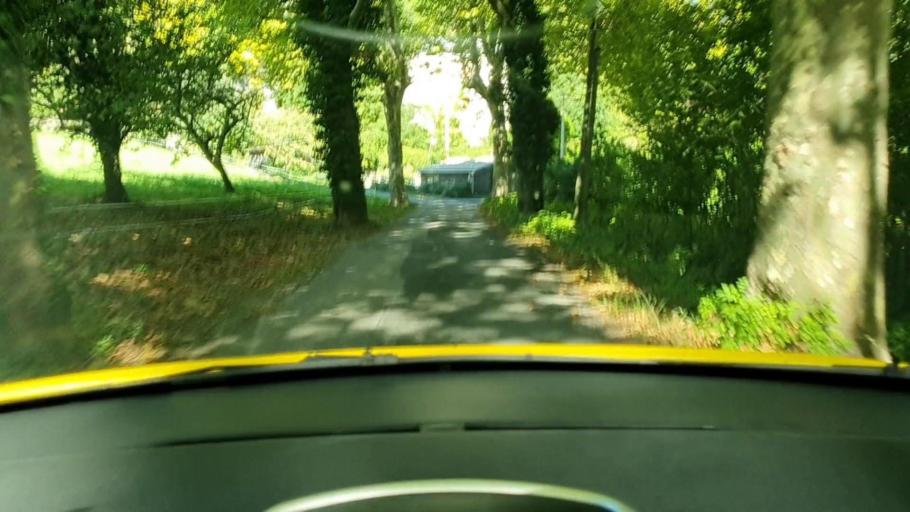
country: FR
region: Languedoc-Roussillon
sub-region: Departement du Gard
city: Le Vigan
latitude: 43.9731
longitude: 3.4383
